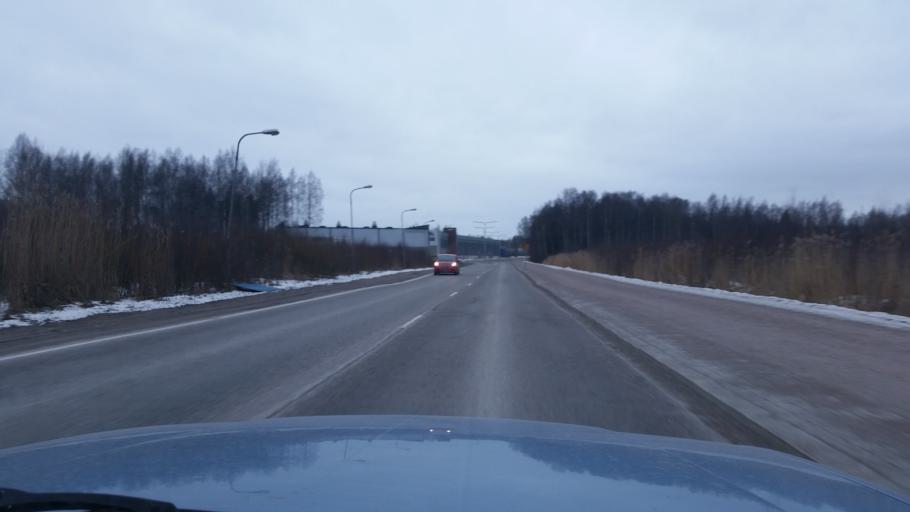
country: FI
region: Uusimaa
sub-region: Helsinki
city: Vantaa
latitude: 60.2512
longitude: 25.0611
